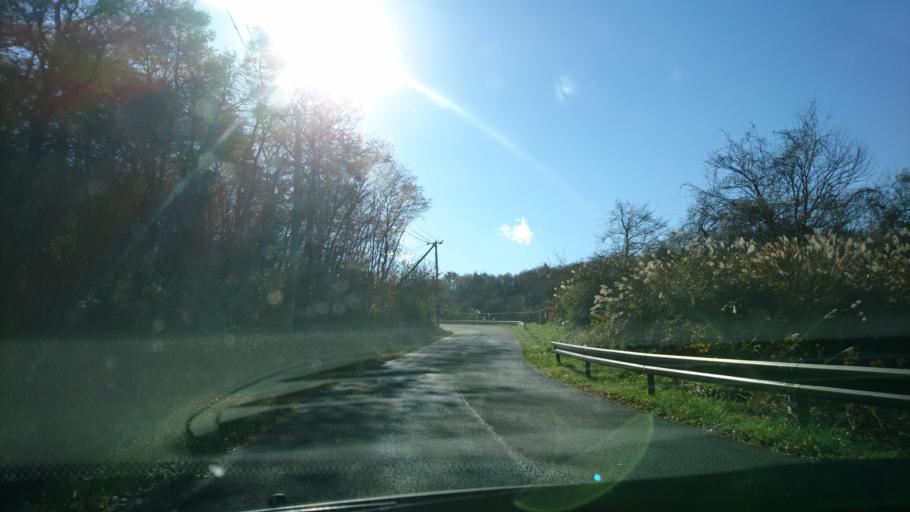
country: JP
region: Iwate
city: Ichinoseki
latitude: 38.9994
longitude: 141.0908
